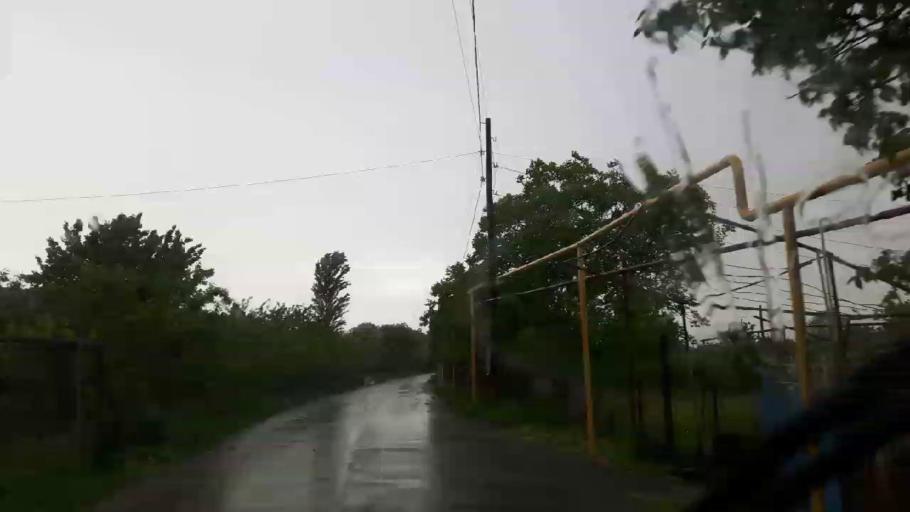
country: GE
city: Agara
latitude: 42.0153
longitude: 43.8474
